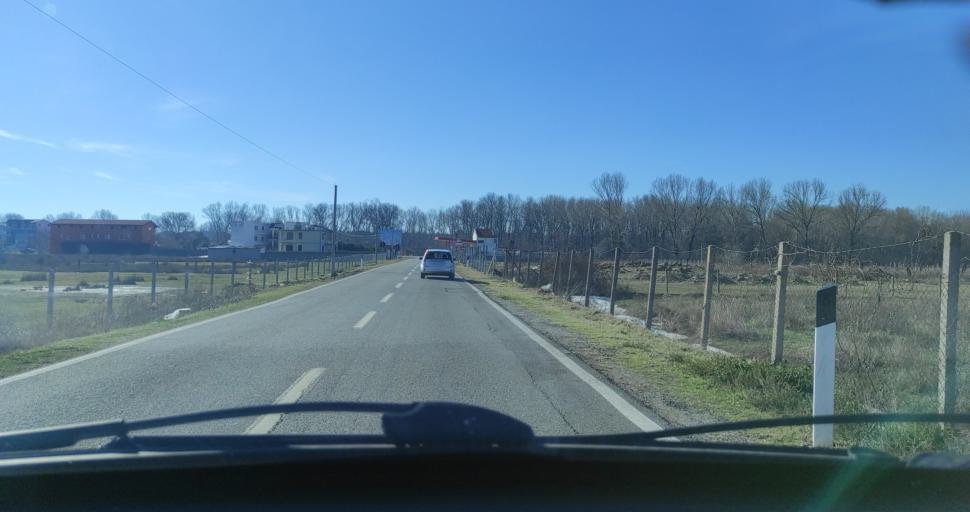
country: AL
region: Shkoder
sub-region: Rrethi i Shkodres
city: Velipoje
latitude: 41.8698
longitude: 19.4042
